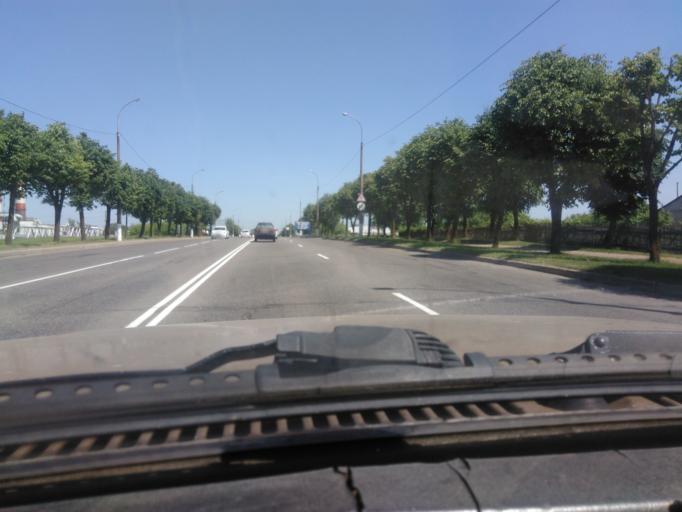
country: BY
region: Mogilev
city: Mahilyow
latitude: 53.9128
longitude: 30.3656
